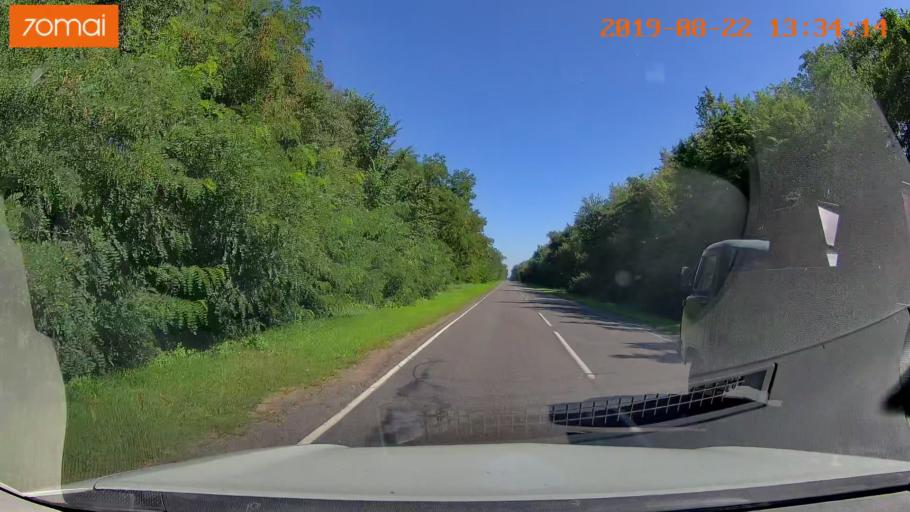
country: BY
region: Minsk
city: Staryya Darohi
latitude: 53.2156
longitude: 28.2370
